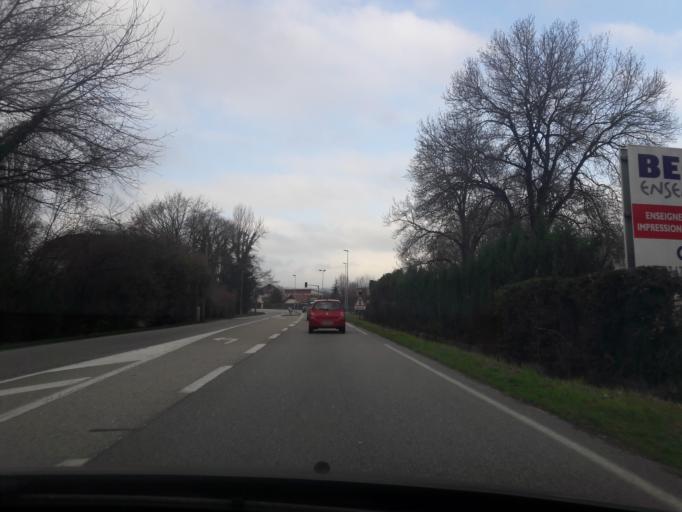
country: FR
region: Rhone-Alpes
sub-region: Departement de l'Isere
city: Saint-Jean-de-Moirans
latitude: 45.3254
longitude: 5.5875
